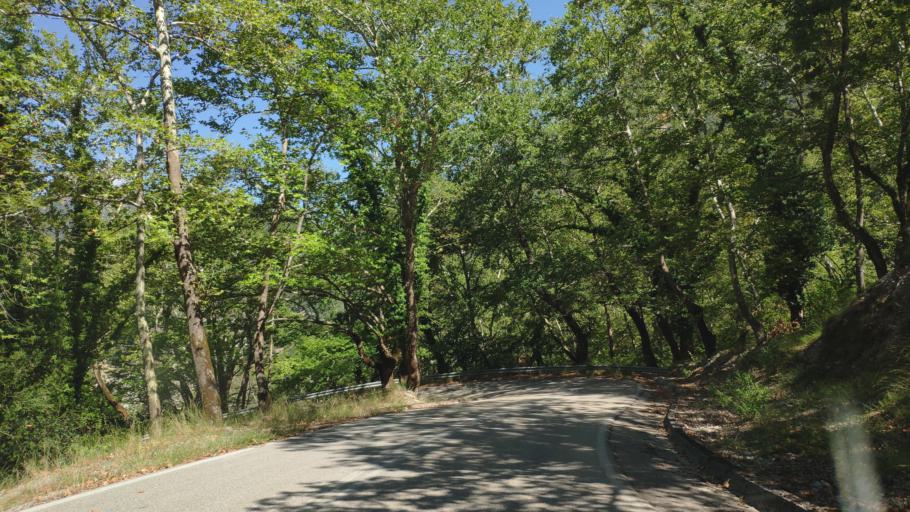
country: GR
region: Central Greece
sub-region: Nomos Evrytanias
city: Kerasochori
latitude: 39.0215
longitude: 21.6011
